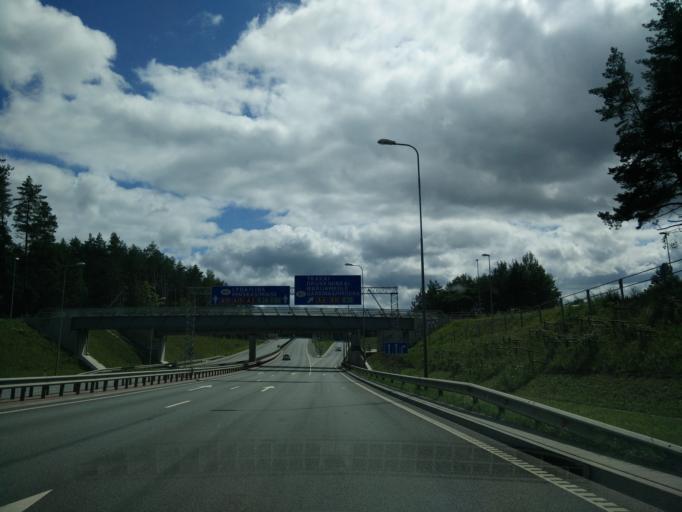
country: LT
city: Baltoji Voke
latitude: 54.6372
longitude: 25.1515
